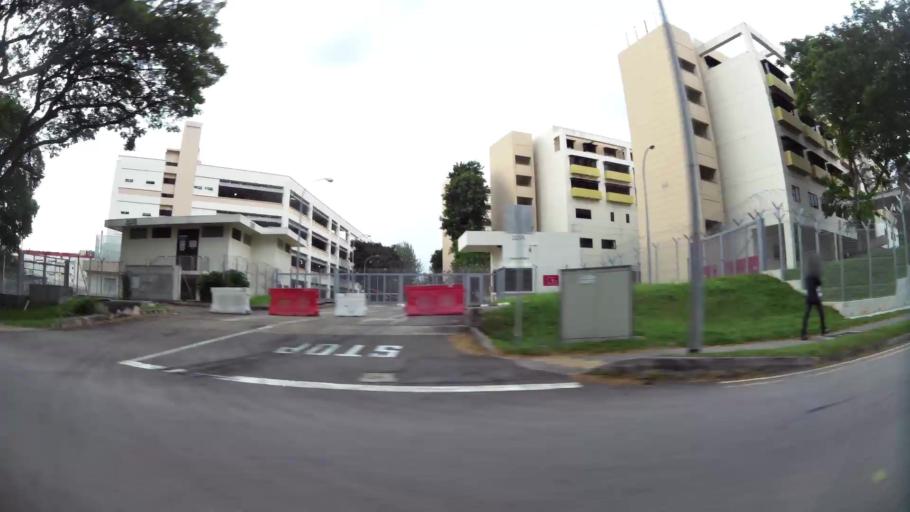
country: MY
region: Johor
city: Johor Bahru
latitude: 1.4641
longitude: 103.8144
